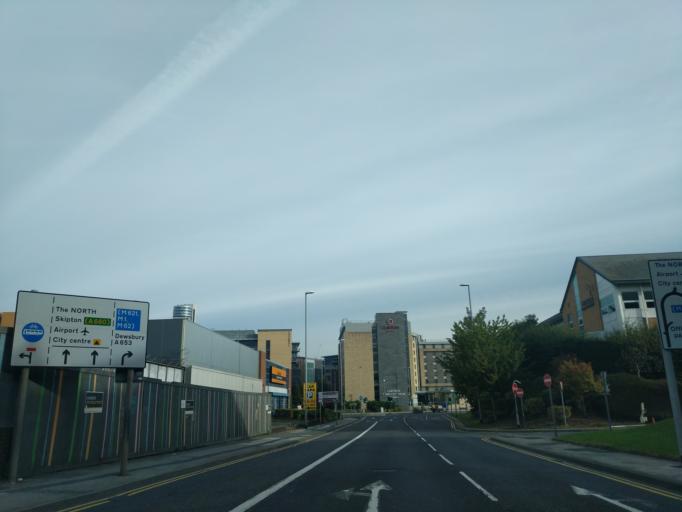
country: GB
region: England
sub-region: City and Borough of Leeds
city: Leeds
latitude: 53.7868
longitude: -1.5478
